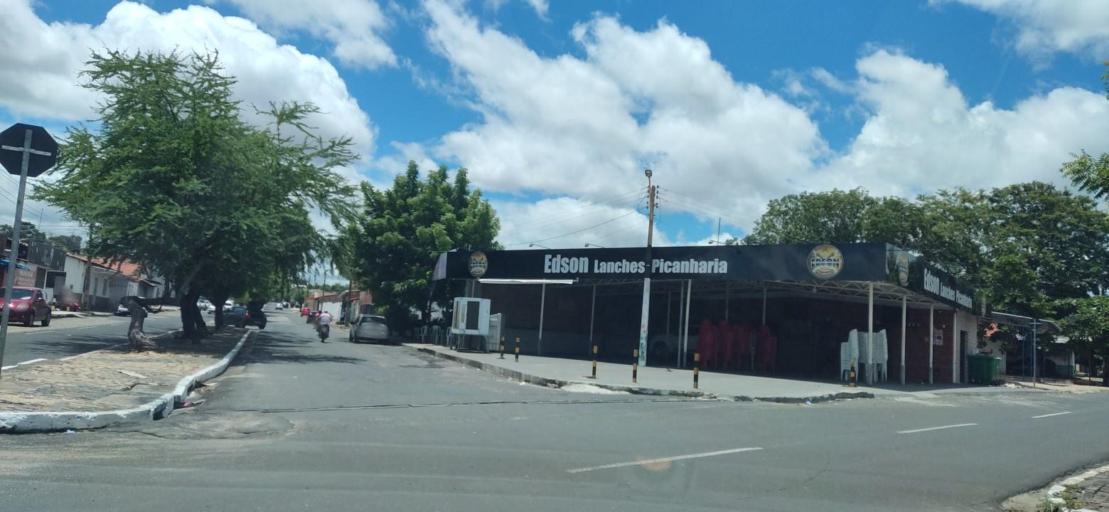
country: BR
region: Piaui
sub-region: Teresina
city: Teresina
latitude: -5.1481
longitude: -42.7804
